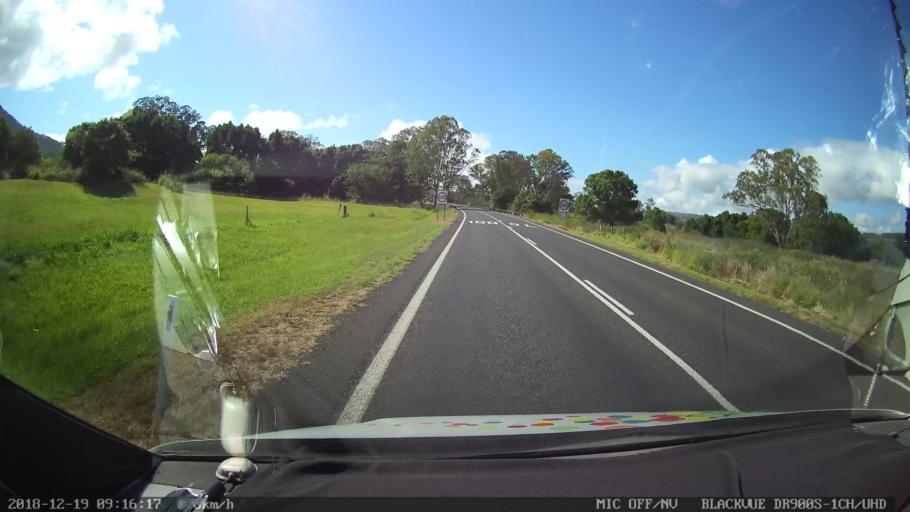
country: AU
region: New South Wales
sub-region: Kyogle
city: Kyogle
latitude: -28.5196
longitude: 152.9664
